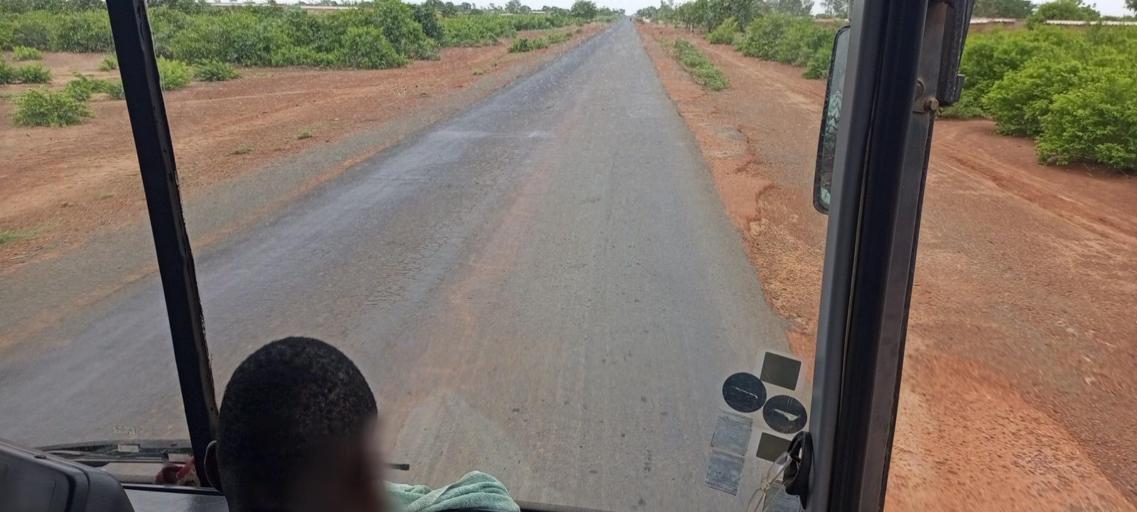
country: ML
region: Sikasso
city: Koutiala
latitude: 12.5411
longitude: -5.5758
